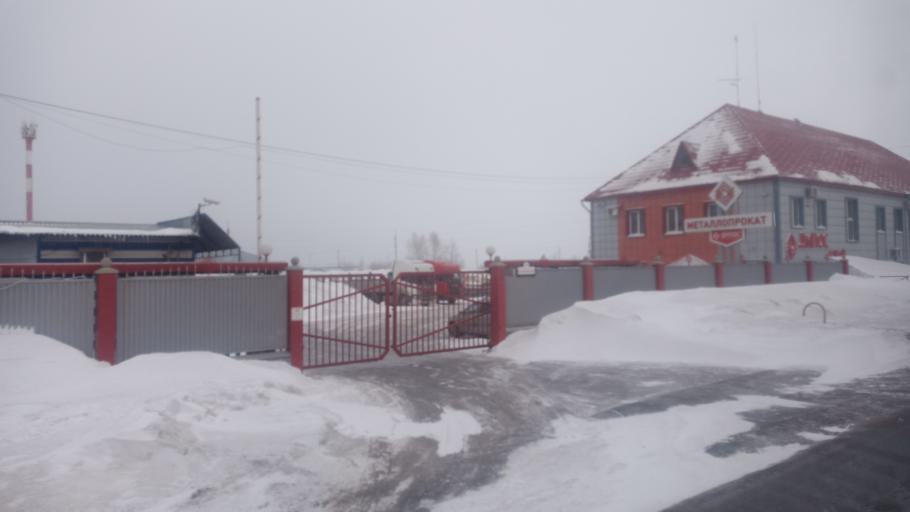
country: RU
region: Altai Krai
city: Novosilikatnyy
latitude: 53.3880
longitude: 83.6560
